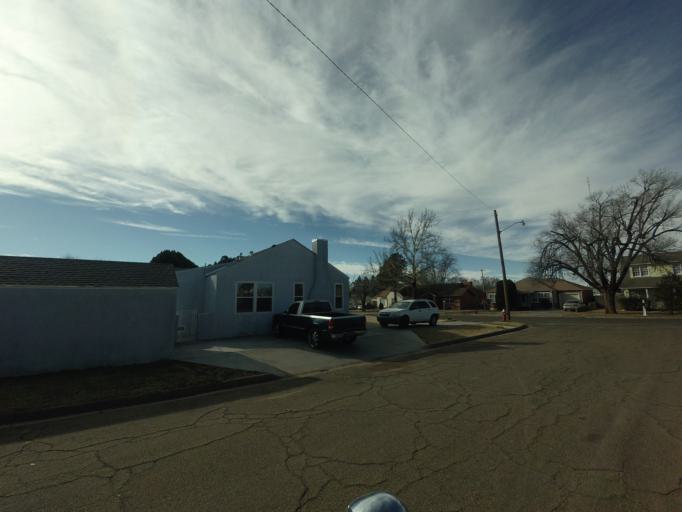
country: US
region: New Mexico
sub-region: Curry County
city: Clovis
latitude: 34.4173
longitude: -103.2025
